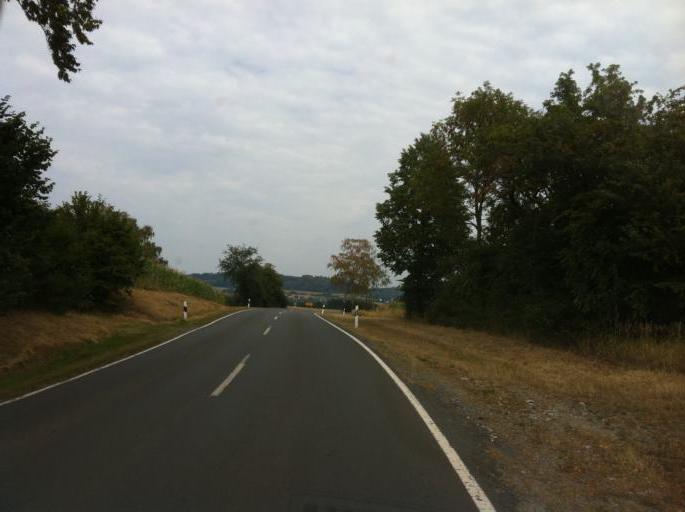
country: DE
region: Bavaria
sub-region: Upper Franconia
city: Goldkronach
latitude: 49.9975
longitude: 11.6629
